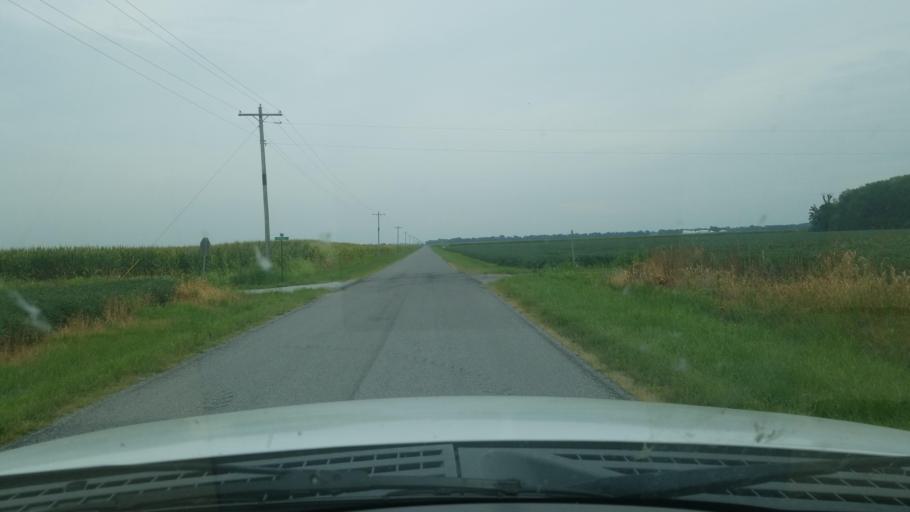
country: US
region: Illinois
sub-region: Saline County
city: Eldorado
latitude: 37.8668
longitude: -88.4762
